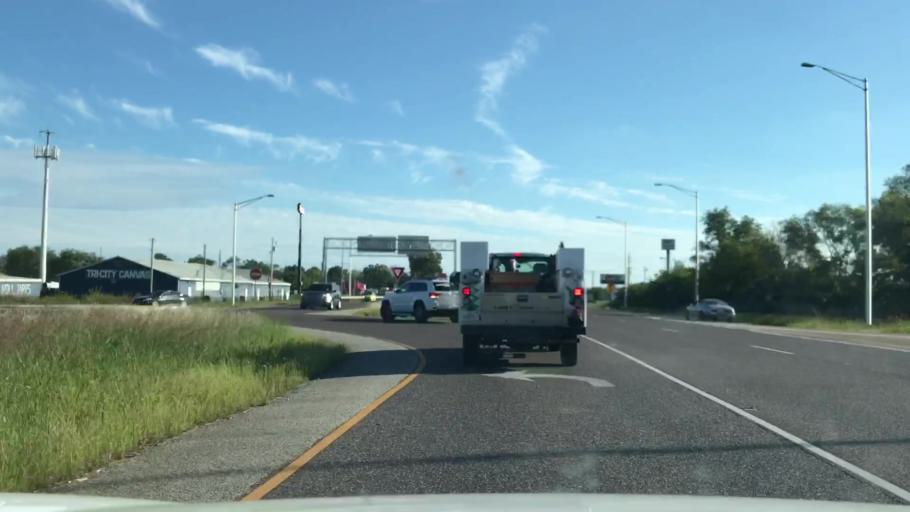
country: US
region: Illinois
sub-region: Madison County
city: Mitchell
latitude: 38.7646
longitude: -90.1244
